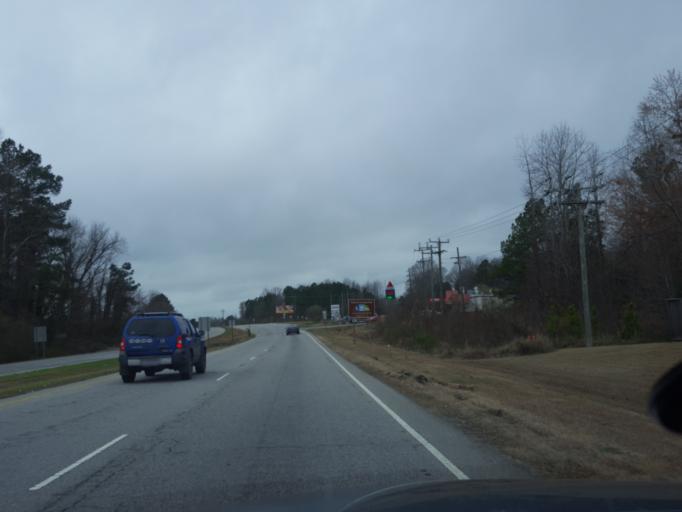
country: US
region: North Carolina
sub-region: Washington County
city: Plymouth
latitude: 35.8086
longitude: -76.8847
